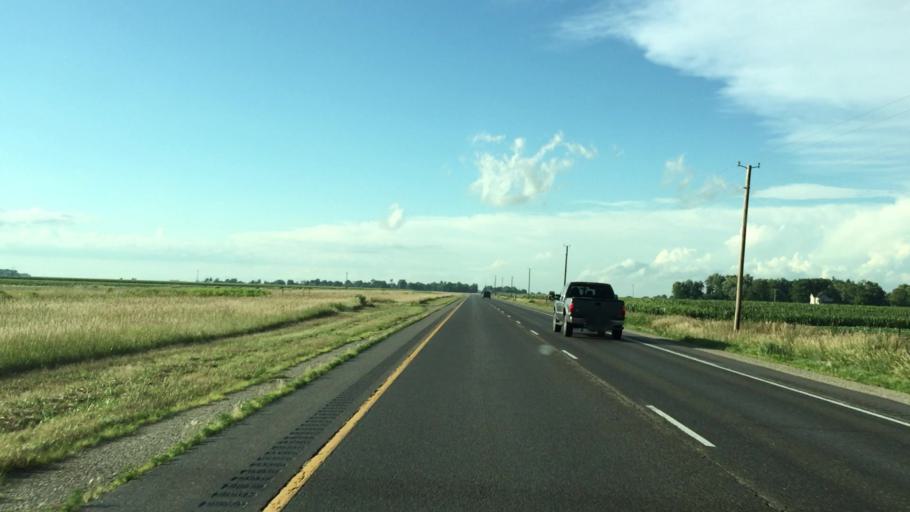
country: US
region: Iowa
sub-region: Henry County
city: Winfield
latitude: 41.0860
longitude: -91.5444
